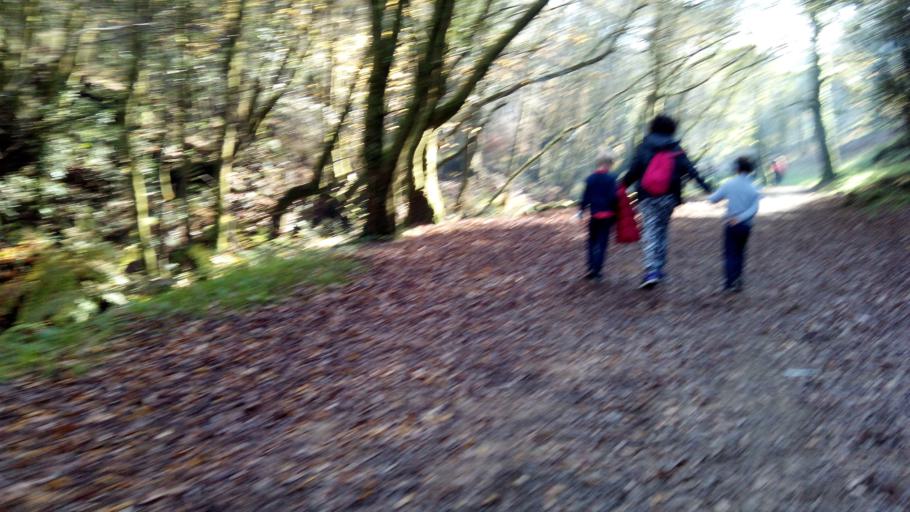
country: ES
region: Galicia
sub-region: Provincia de Pontevedra
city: Meis
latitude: 42.4854
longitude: -8.7452
